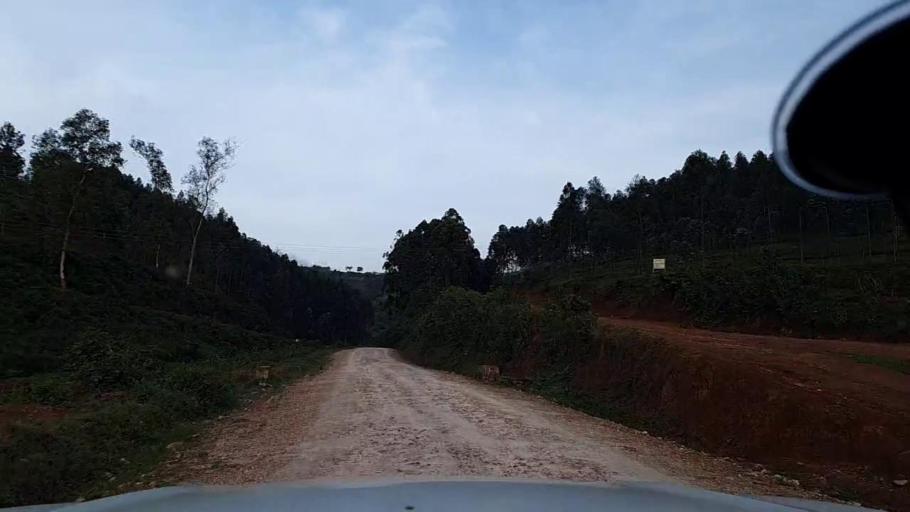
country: RW
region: Southern Province
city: Nyanza
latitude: -2.2150
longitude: 29.6268
